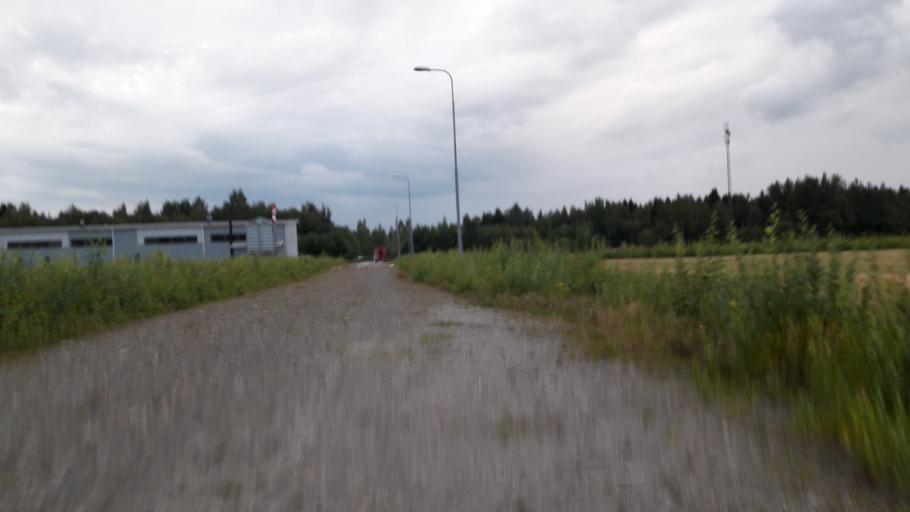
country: FI
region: North Karelia
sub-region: Joensuu
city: Joensuu
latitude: 62.5498
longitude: 29.8378
